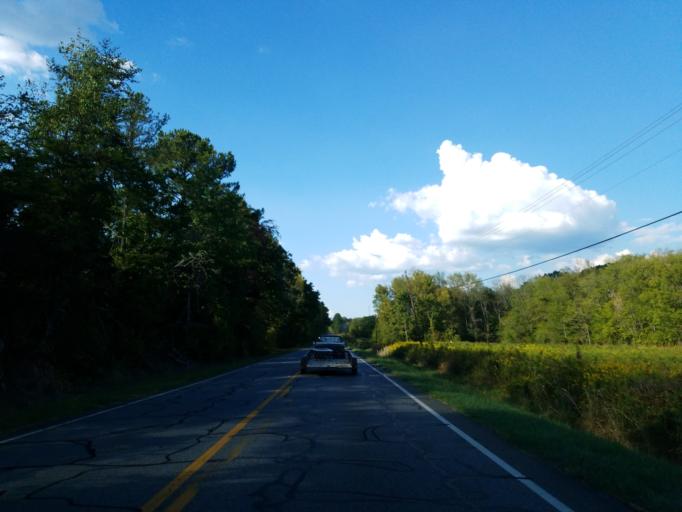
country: US
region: Georgia
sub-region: Bartow County
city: Rydal
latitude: 34.5512
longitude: -84.7074
